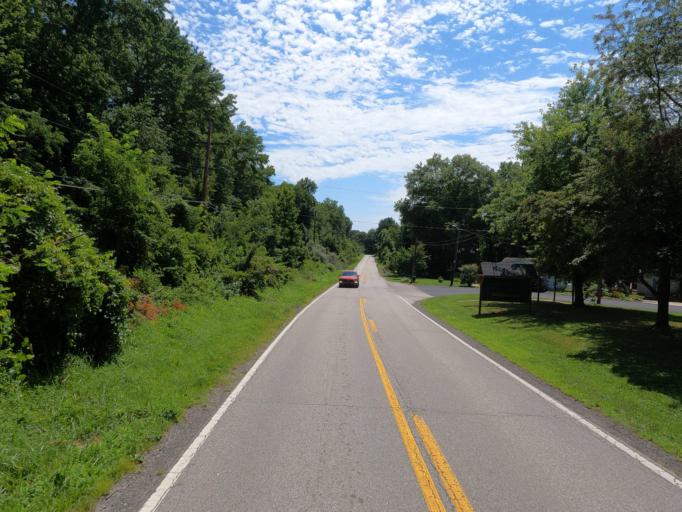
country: US
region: Maryland
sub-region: Cecil County
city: Elkton
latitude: 39.5226
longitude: -75.7967
